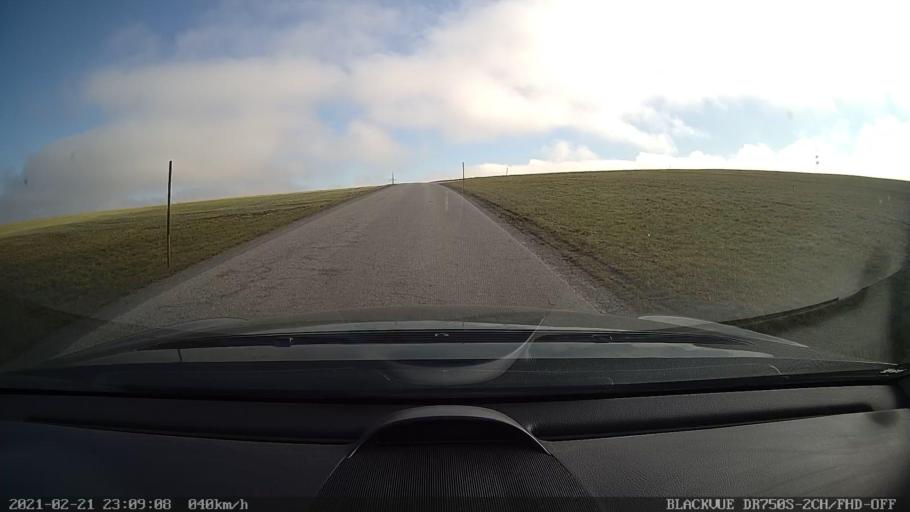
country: DE
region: Bavaria
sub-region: Upper Bavaria
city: Griesstatt
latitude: 47.9958
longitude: 12.1905
